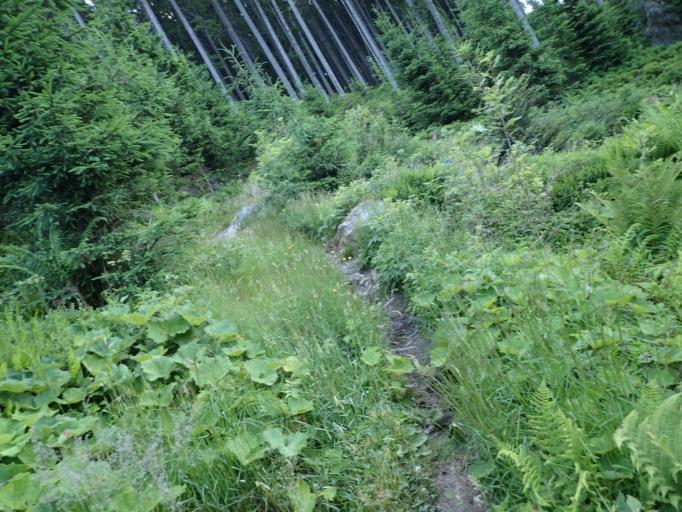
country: AT
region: Salzburg
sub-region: Politischer Bezirk Sankt Johann im Pongau
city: Radstadt
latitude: 47.4450
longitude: 13.4465
